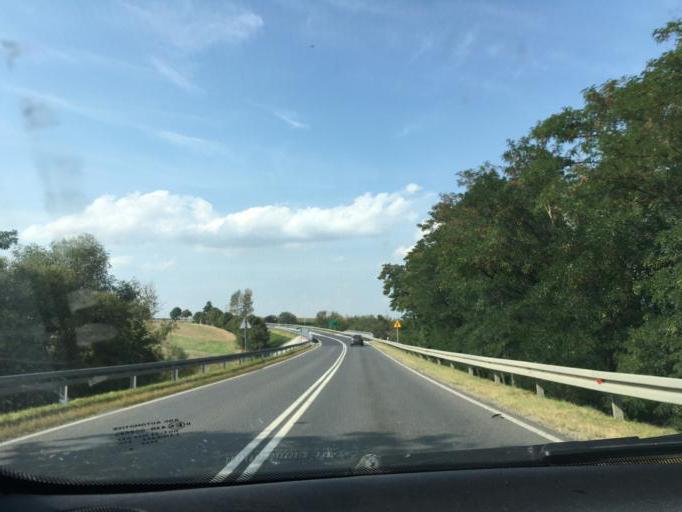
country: PL
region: Opole Voivodeship
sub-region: Powiat prudnicki
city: Laka Prudnicka
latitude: 50.4051
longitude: 17.5098
